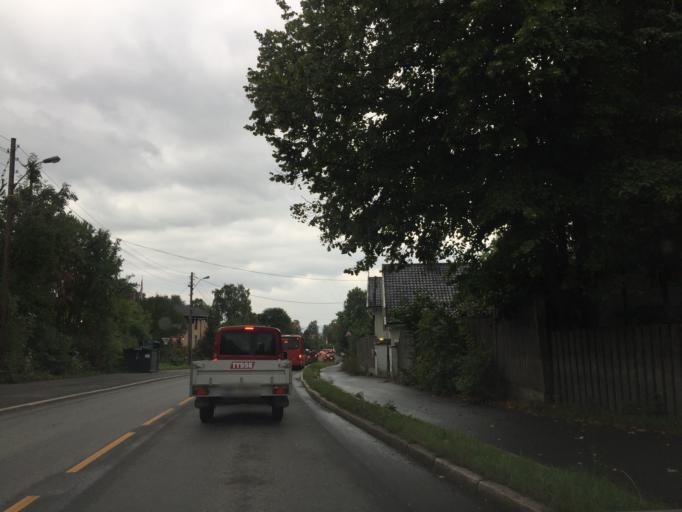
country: NO
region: Oslo
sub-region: Oslo
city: Sjolyststranda
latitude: 59.9426
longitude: 10.6815
